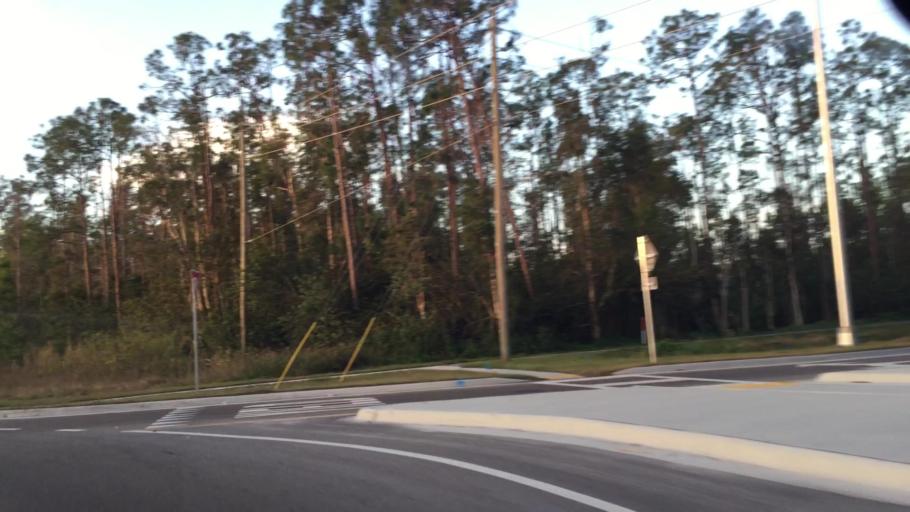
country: US
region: Florida
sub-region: Lee County
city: Villas
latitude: 26.5648
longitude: -81.8472
